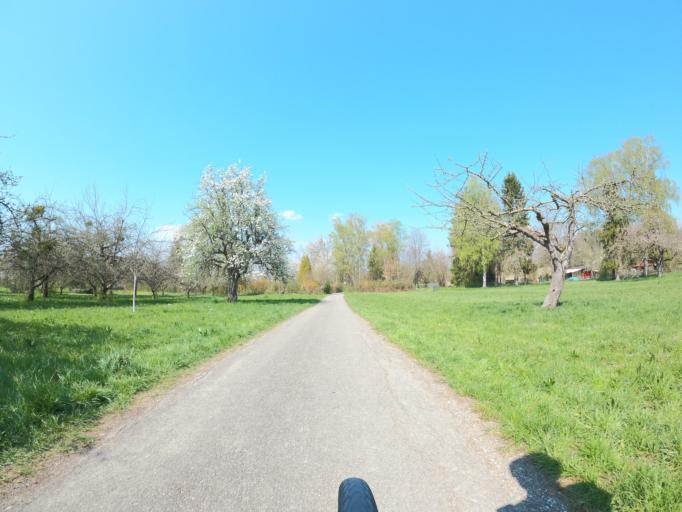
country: DE
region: Baden-Wuerttemberg
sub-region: Tuebingen Region
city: Reutlingen
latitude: 48.4882
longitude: 9.1794
